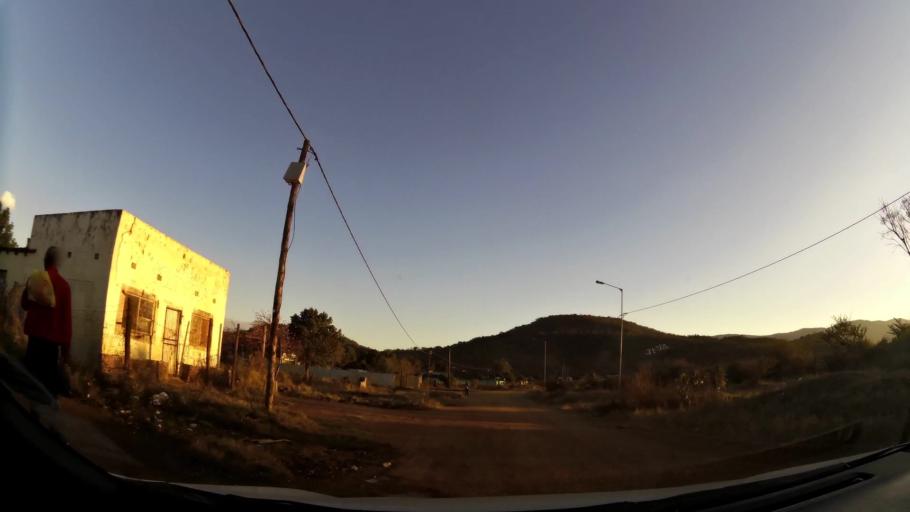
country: ZA
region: Limpopo
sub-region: Waterberg District Municipality
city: Mokopane
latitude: -24.1445
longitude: 28.9737
